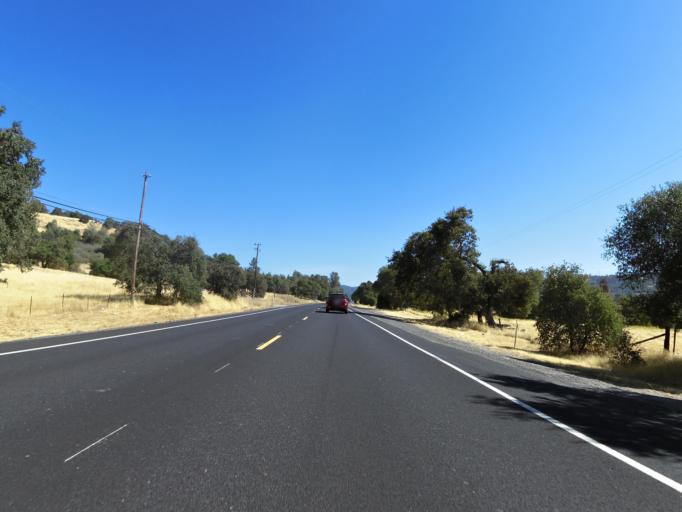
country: US
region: California
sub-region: Calaveras County
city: Murphys
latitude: 38.1047
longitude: -120.4663
